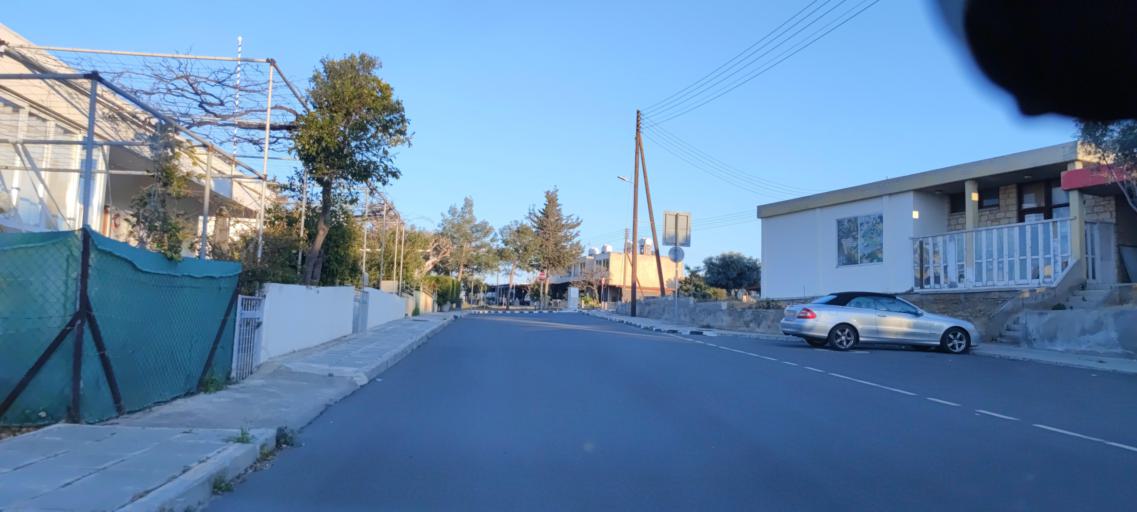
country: CY
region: Pafos
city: Paphos
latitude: 34.7834
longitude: 32.4140
